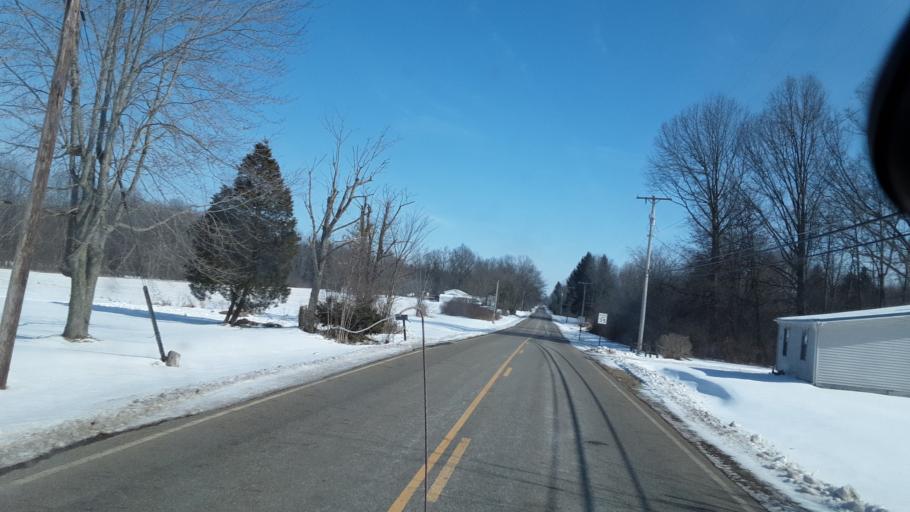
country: US
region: Ohio
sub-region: Stark County
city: Alliance
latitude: 40.9620
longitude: -81.0914
